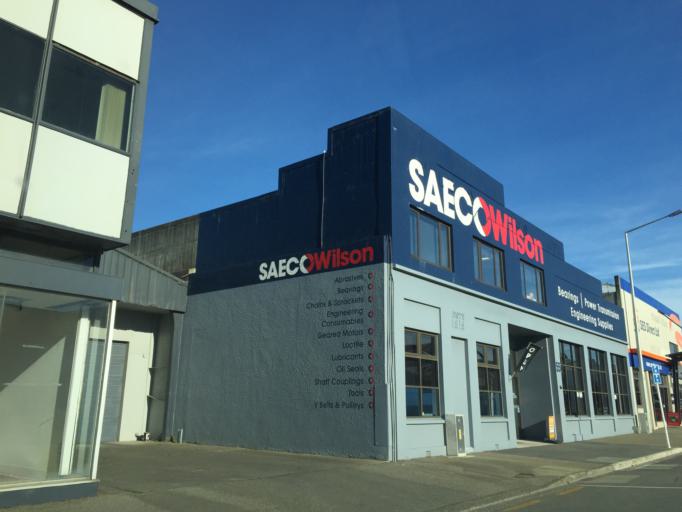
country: NZ
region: Southland
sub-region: Invercargill City
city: Invercargill
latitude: -46.4075
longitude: 168.3501
